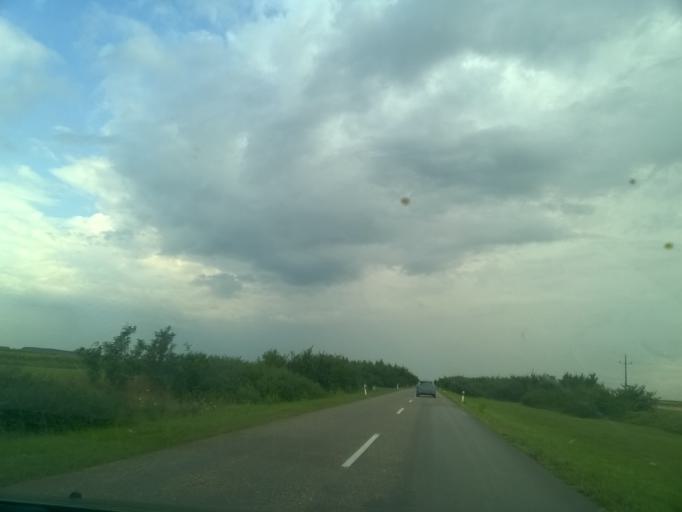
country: RS
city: Uzdin
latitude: 45.2354
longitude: 20.6269
